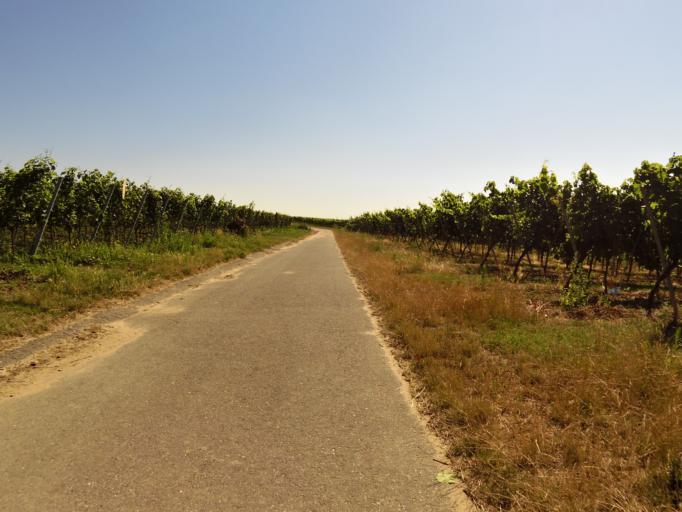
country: DE
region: Rheinland-Pfalz
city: Freinsheim
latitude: 49.5194
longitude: 8.2039
